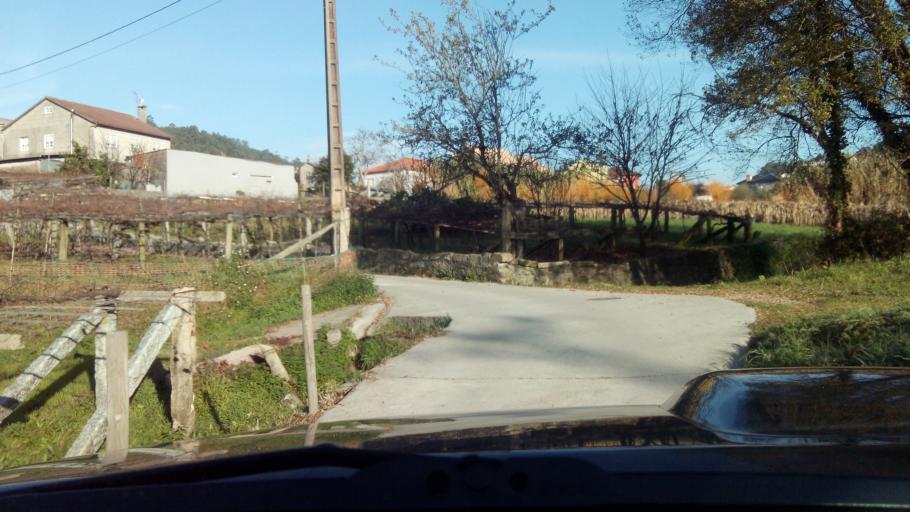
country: ES
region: Galicia
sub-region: Provincia de Pontevedra
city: Marin
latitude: 42.3619
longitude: -8.7029
